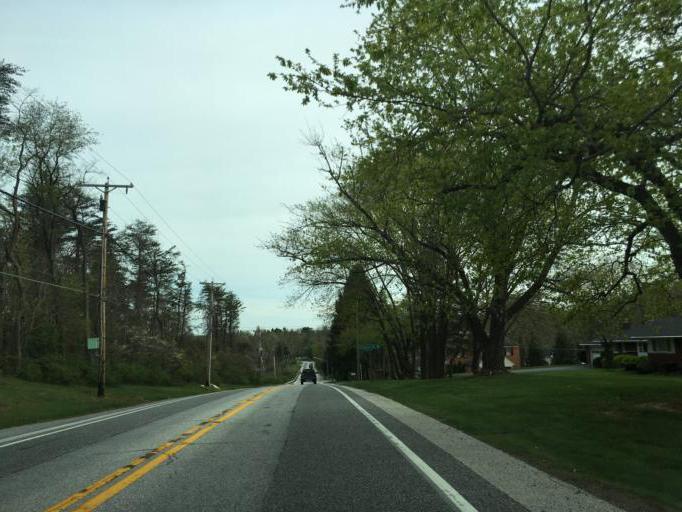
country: US
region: Maryland
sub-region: Baltimore County
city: Hampton
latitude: 39.4363
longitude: -76.5969
